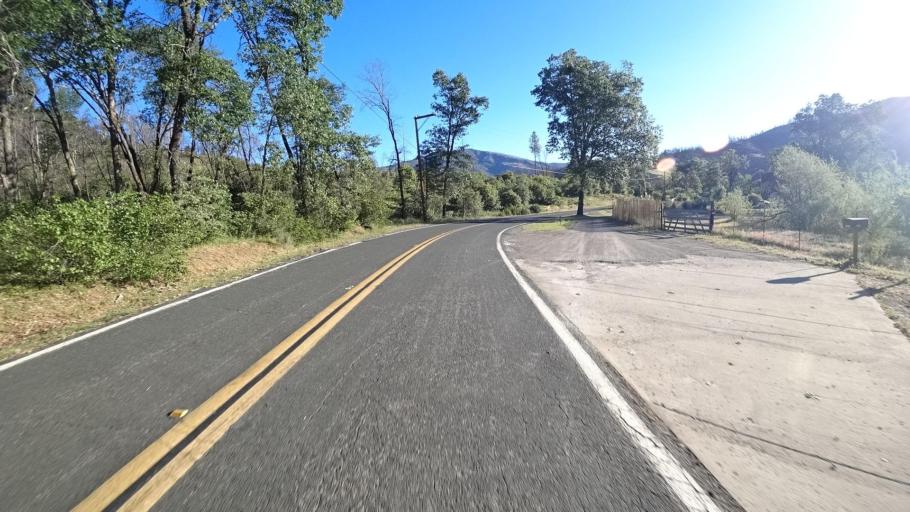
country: US
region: California
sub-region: Lake County
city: Upper Lake
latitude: 39.2344
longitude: -122.9464
